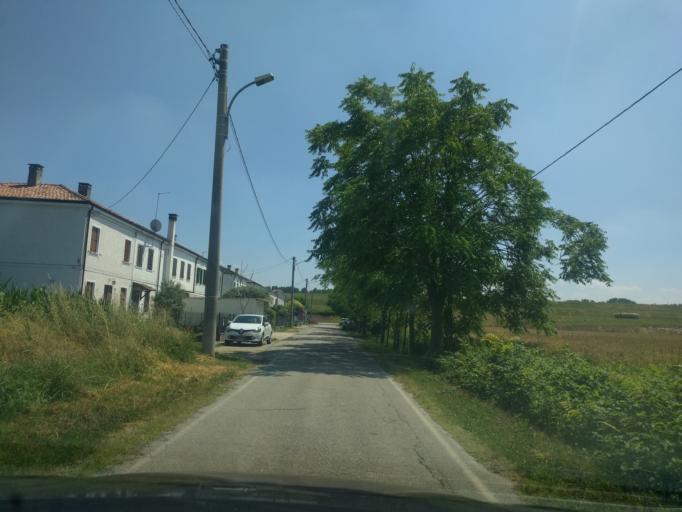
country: IT
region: Veneto
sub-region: Provincia di Rovigo
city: Guarda Veneta
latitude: 44.9809
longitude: 11.8166
